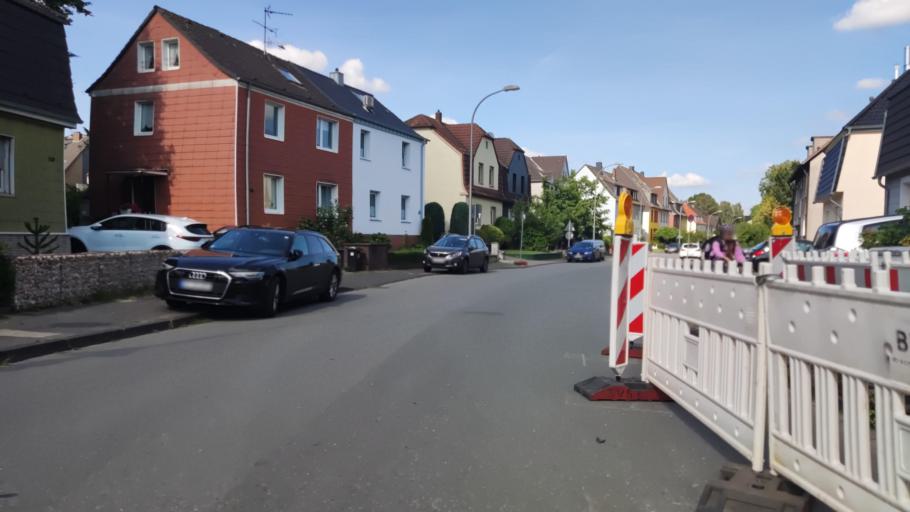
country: DE
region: North Rhine-Westphalia
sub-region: Regierungsbezirk Arnsberg
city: Bochum
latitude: 51.4657
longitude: 7.2373
